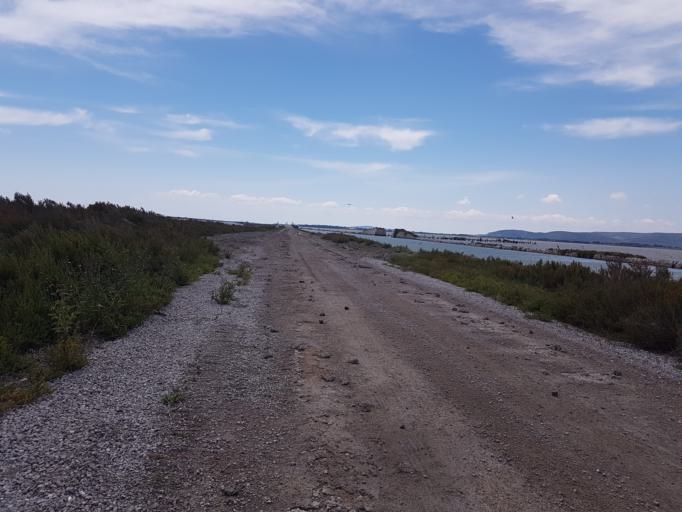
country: FR
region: Languedoc-Roussillon
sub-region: Departement de l'Herault
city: Villeneuve-les-Maguelone
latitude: 43.4933
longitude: 3.8496
